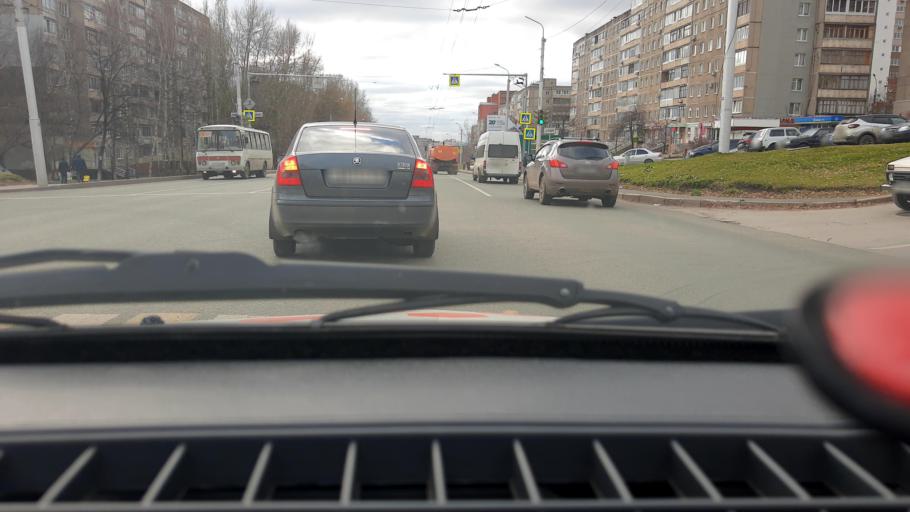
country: RU
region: Bashkortostan
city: Ufa
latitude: 54.7039
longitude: 55.9972
